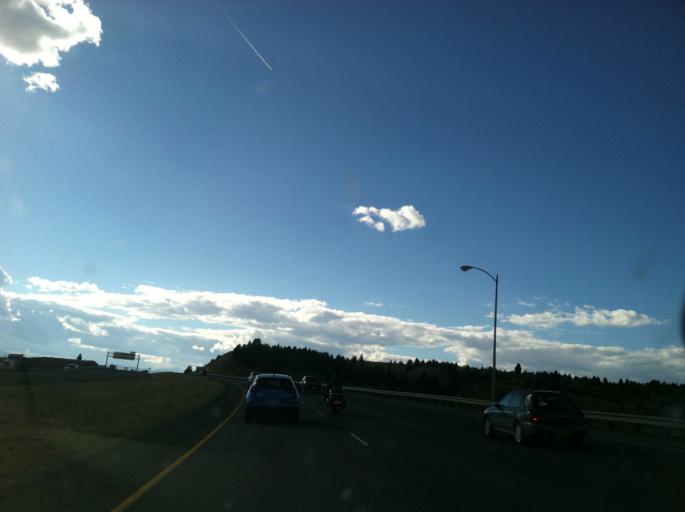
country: US
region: Montana
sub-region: Silver Bow County
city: Butte
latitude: 46.0054
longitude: -112.5755
